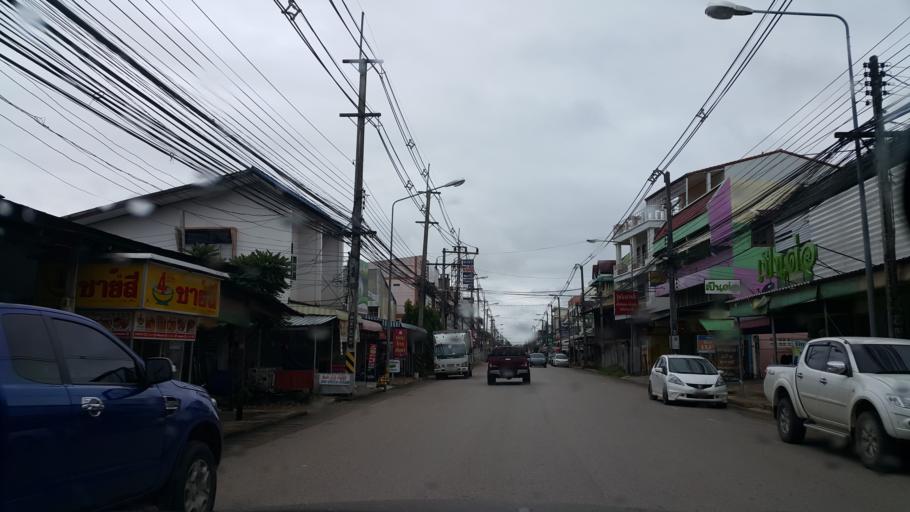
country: TH
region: Phayao
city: Chiang Kham
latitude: 19.5272
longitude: 100.3024
